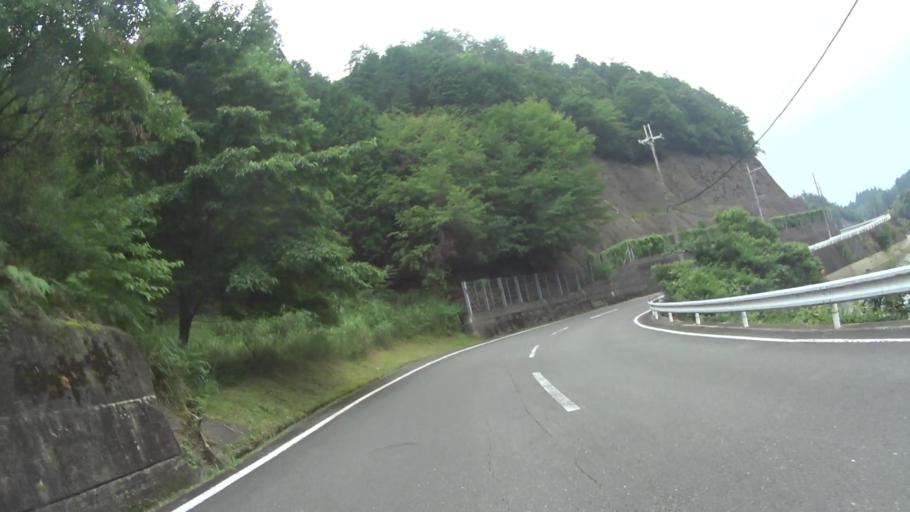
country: JP
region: Kyoto
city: Kameoka
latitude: 35.0957
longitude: 135.6026
